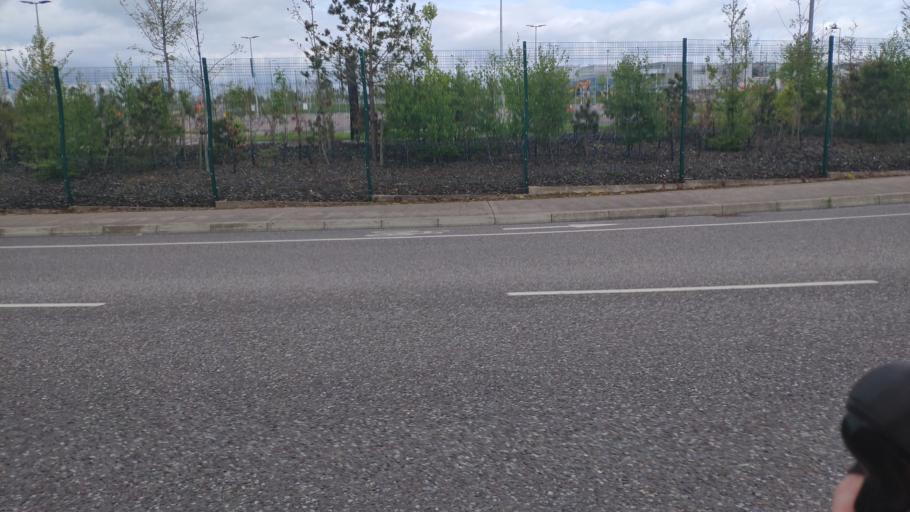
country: IE
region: Munster
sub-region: County Cork
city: Cork
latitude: 51.9052
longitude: -8.5178
